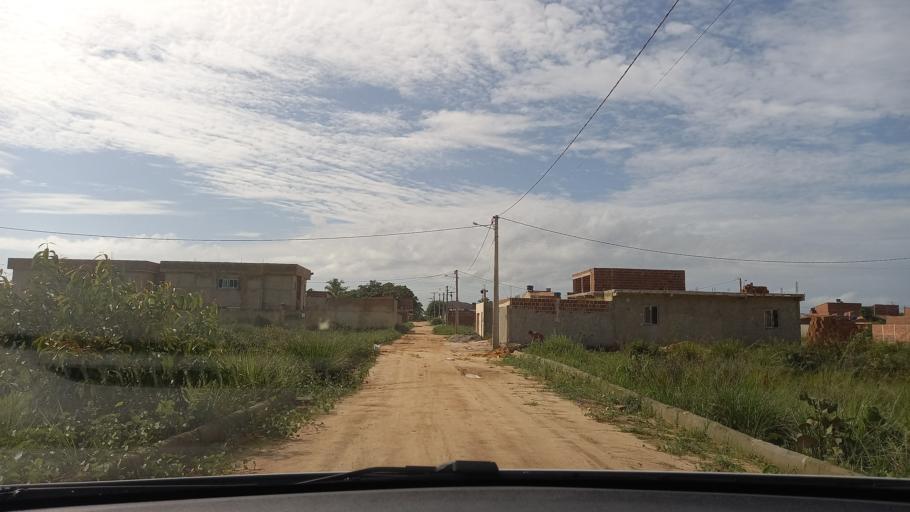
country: BR
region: Pernambuco
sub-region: Sao Jose Da Coroa Grande
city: Sao Jose da Coroa Grande
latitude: -8.9198
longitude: -35.1677
